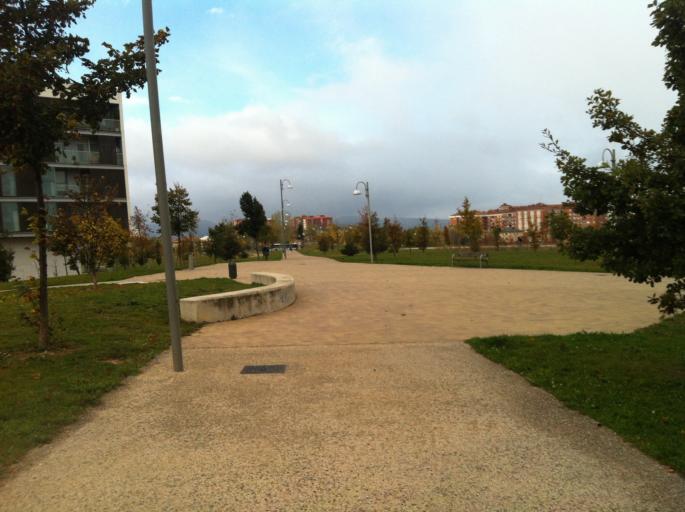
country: ES
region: Basque Country
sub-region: Provincia de Alava
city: Gasteiz / Vitoria
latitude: 42.8496
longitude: -2.6967
